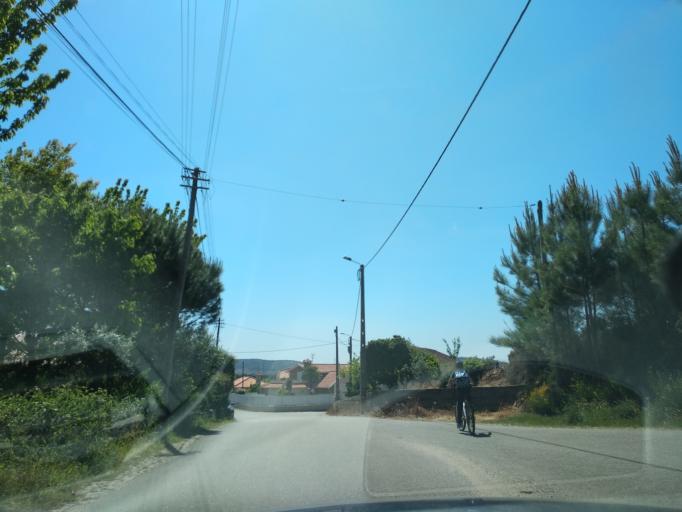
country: PT
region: Porto
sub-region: Paredes
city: Gandra
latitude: 41.1829
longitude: -8.4204
